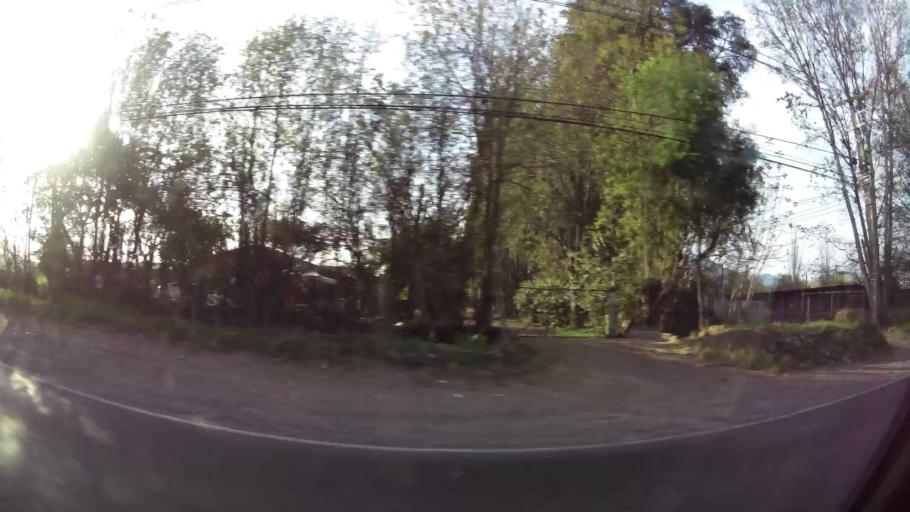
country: CL
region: Santiago Metropolitan
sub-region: Provincia de Maipo
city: San Bernardo
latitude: -33.5618
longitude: -70.7593
